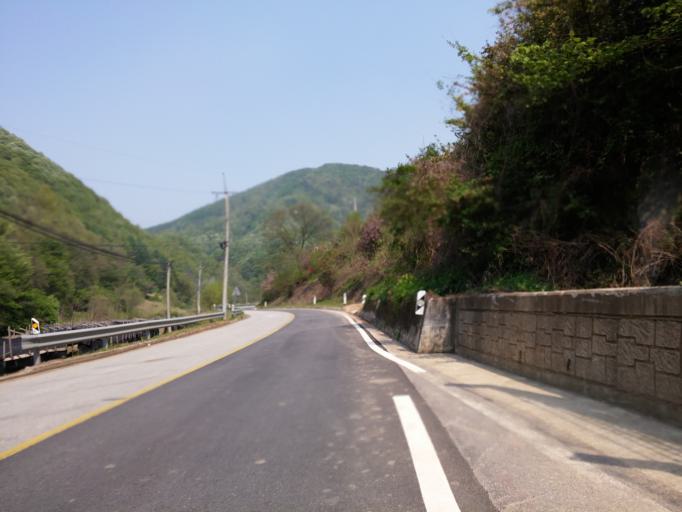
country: KR
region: Chungcheongbuk-do
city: Okcheon
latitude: 36.3977
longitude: 127.6033
